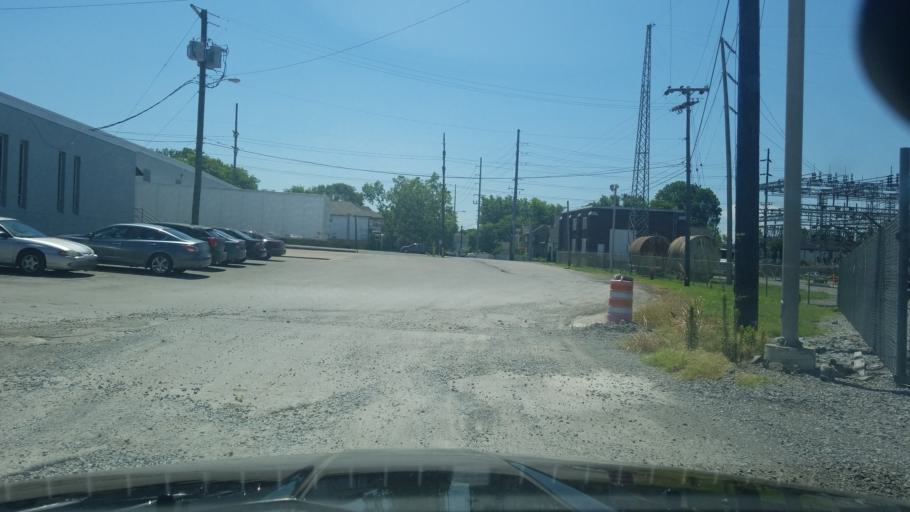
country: US
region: Tennessee
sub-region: Davidson County
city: Belle Meade
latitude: 36.1666
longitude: -86.8661
